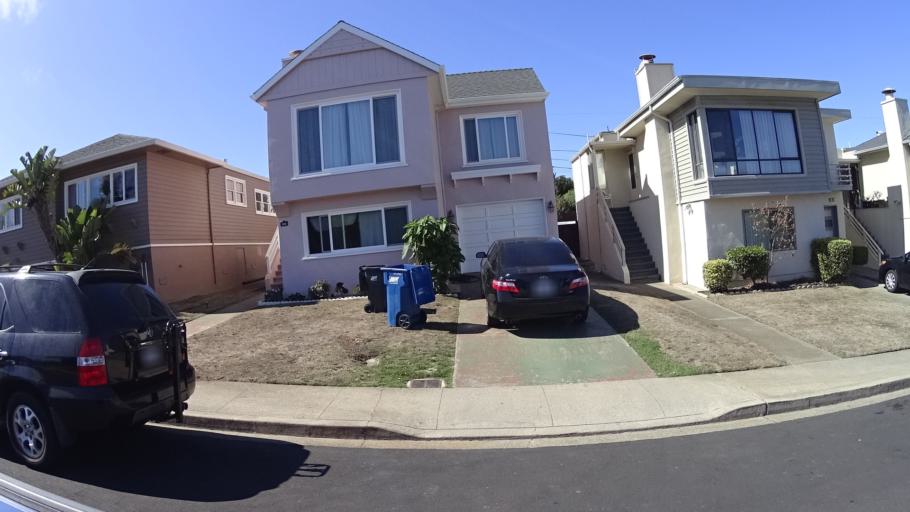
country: US
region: California
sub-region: San Mateo County
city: Broadmoor
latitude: 37.6936
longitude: -122.4921
